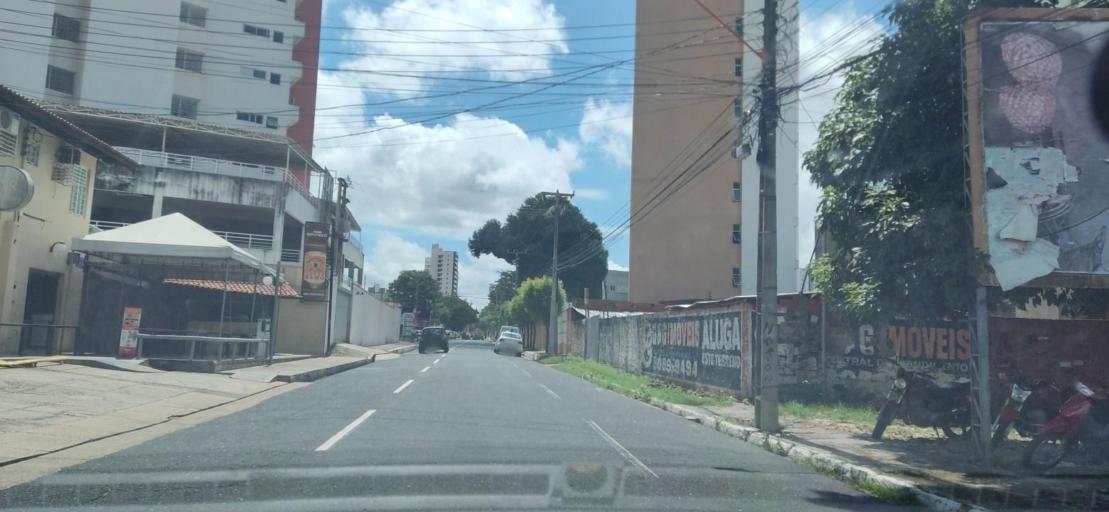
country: BR
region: Piaui
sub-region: Teresina
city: Teresina
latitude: -5.0643
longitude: -42.7871
